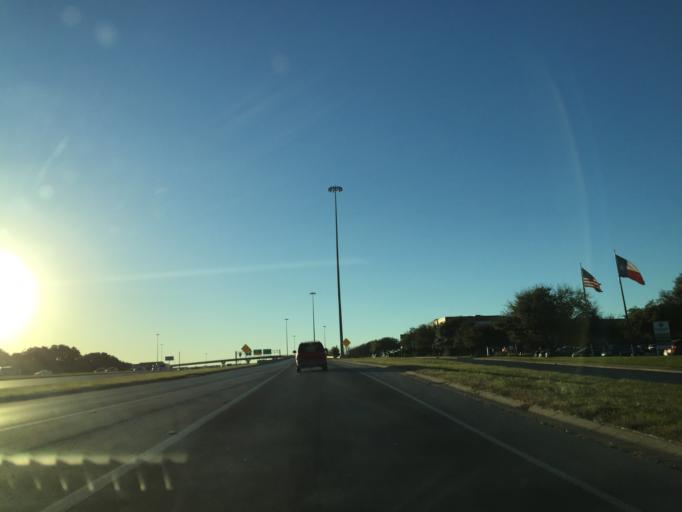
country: US
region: Texas
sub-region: Travis County
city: Austin
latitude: 30.3220
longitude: -97.6983
